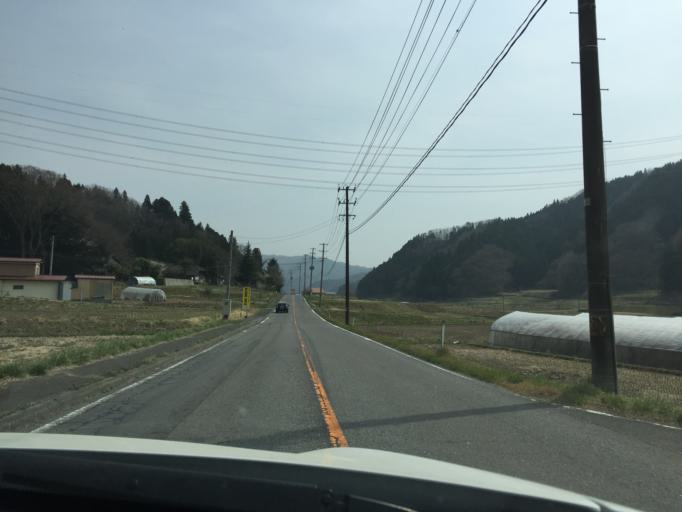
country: JP
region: Fukushima
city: Ishikawa
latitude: 37.1036
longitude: 140.5085
